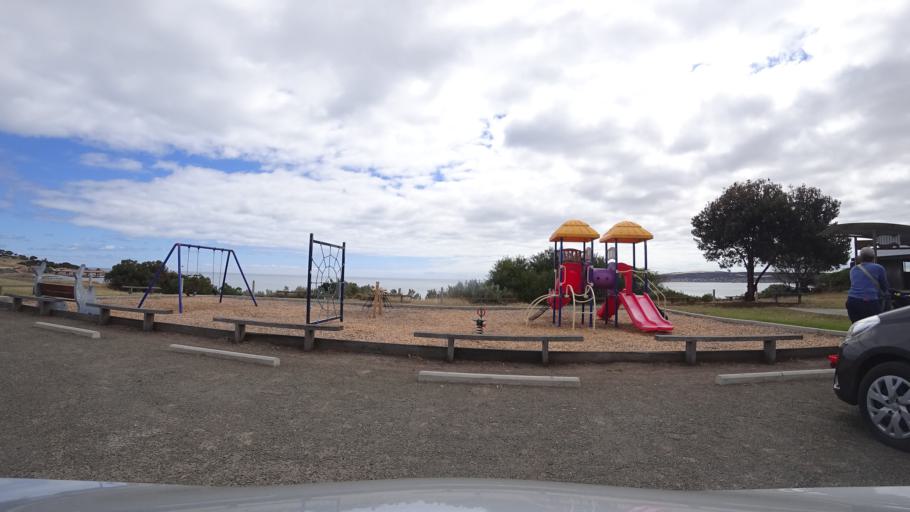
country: AU
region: South Australia
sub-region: Kangaroo Island
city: Kingscote
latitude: -35.5939
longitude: 137.5066
